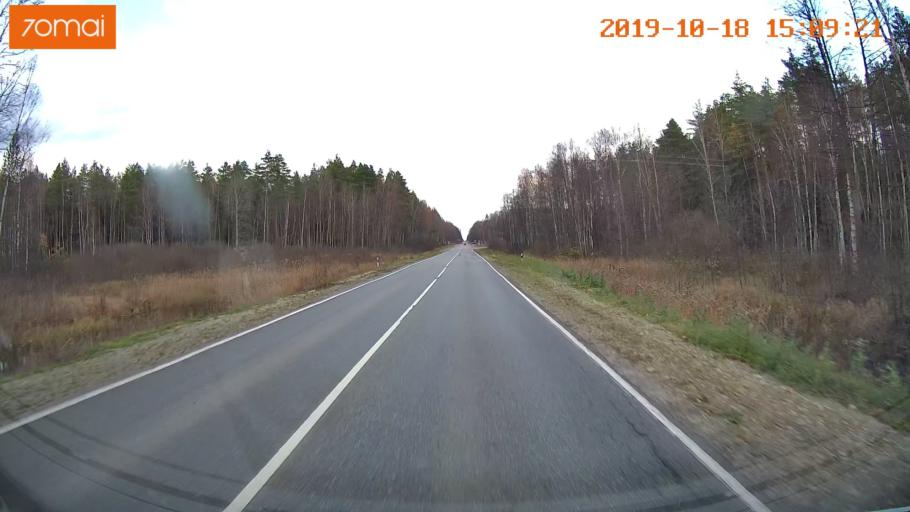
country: RU
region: Vladimir
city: Gus'-Khrustal'nyy
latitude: 55.5652
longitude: 40.6204
